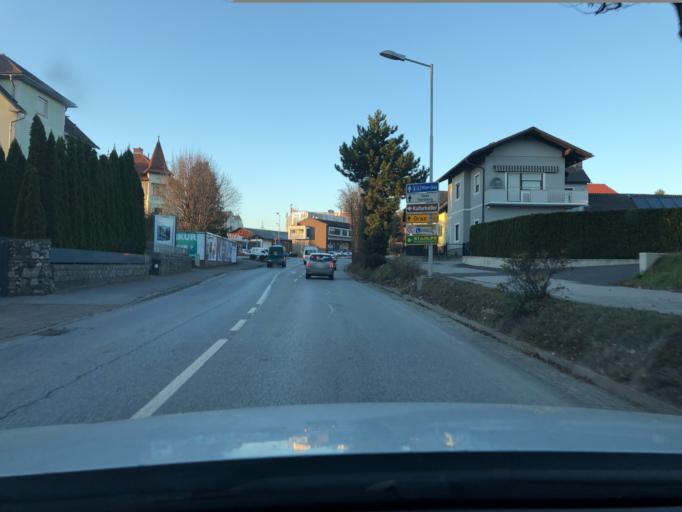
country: AT
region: Styria
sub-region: Politischer Bezirk Weiz
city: Gleisdorf
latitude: 47.1083
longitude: 15.7079
